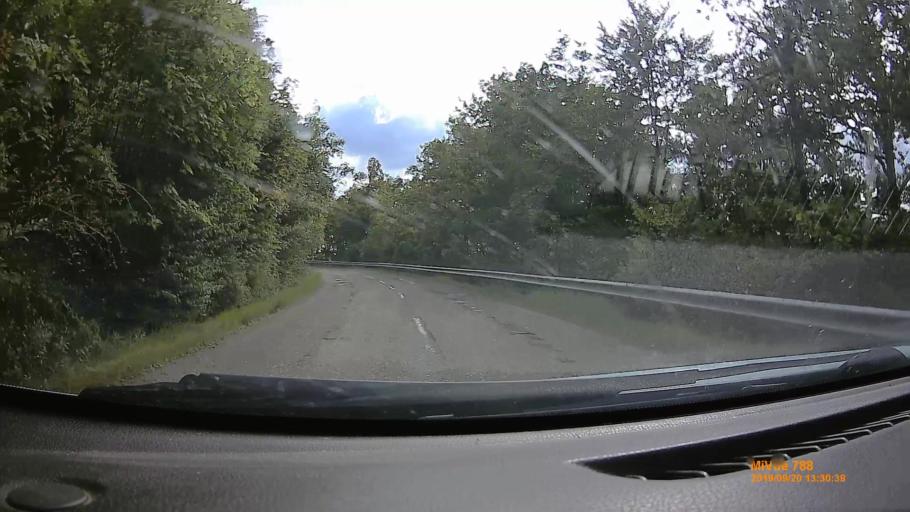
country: HU
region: Heves
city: Szilvasvarad
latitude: 48.0558
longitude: 20.4865
